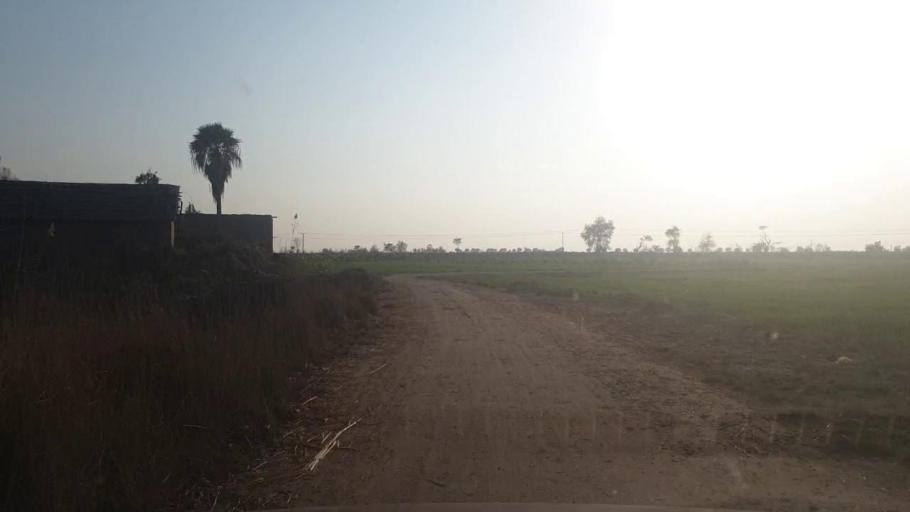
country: PK
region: Sindh
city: Sakrand
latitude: 26.0766
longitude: 68.3987
